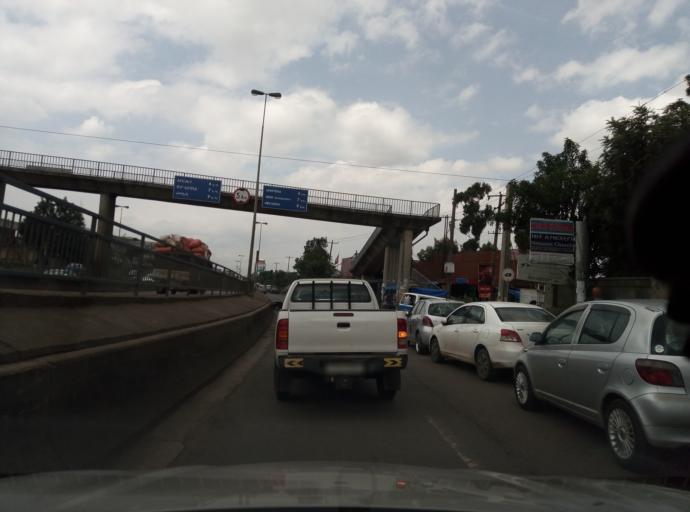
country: ET
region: Adis Abeba
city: Addis Ababa
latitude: 9.0060
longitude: 38.7186
